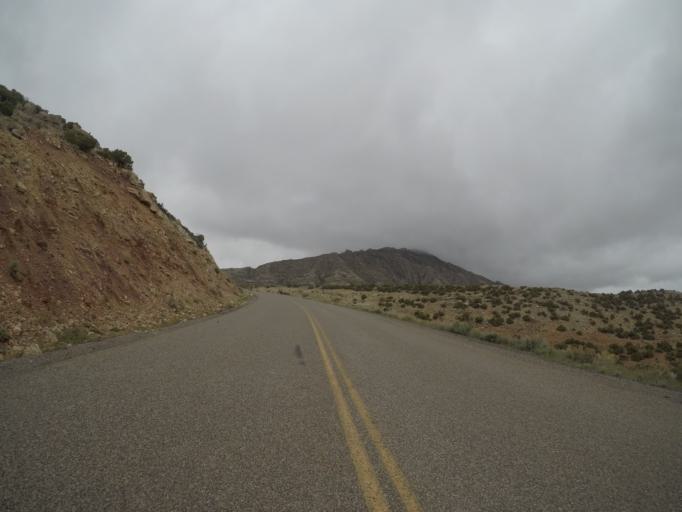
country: US
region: Wyoming
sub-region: Big Horn County
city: Lovell
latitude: 45.0257
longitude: -108.2630
